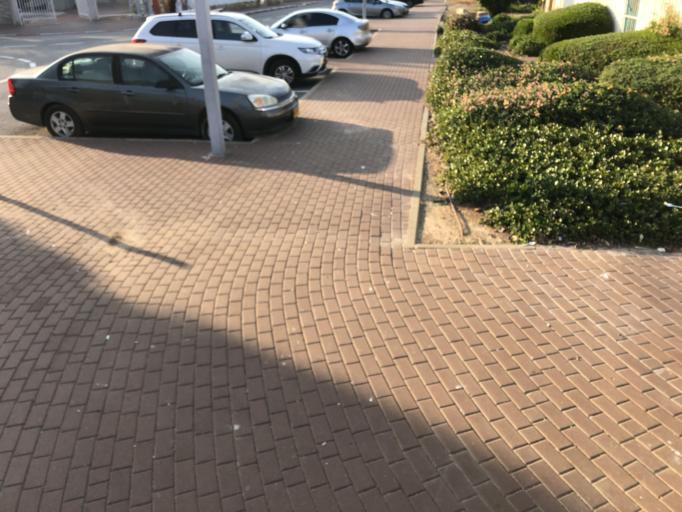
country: IL
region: Northern District
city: `Akko
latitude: 32.9265
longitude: 35.0890
